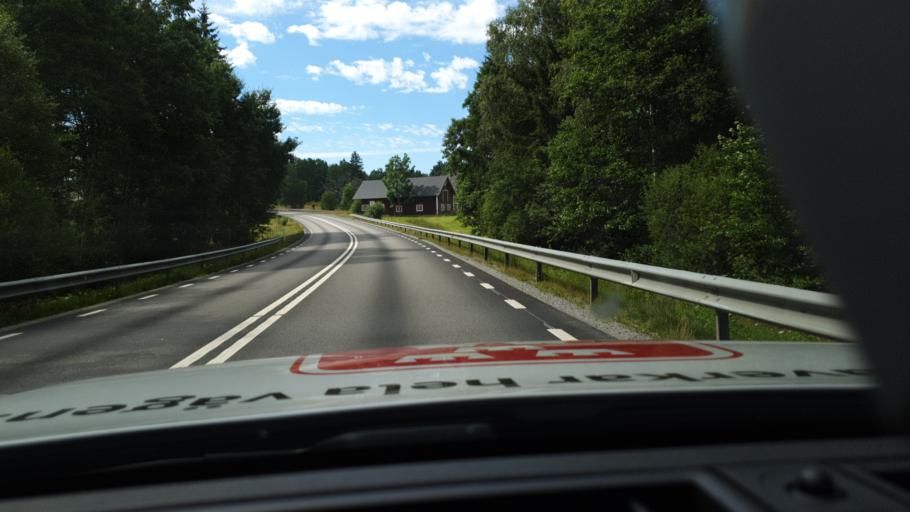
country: SE
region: Joenkoeping
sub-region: Savsjo Kommun
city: Stockaryd
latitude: 57.2552
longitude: 14.5191
